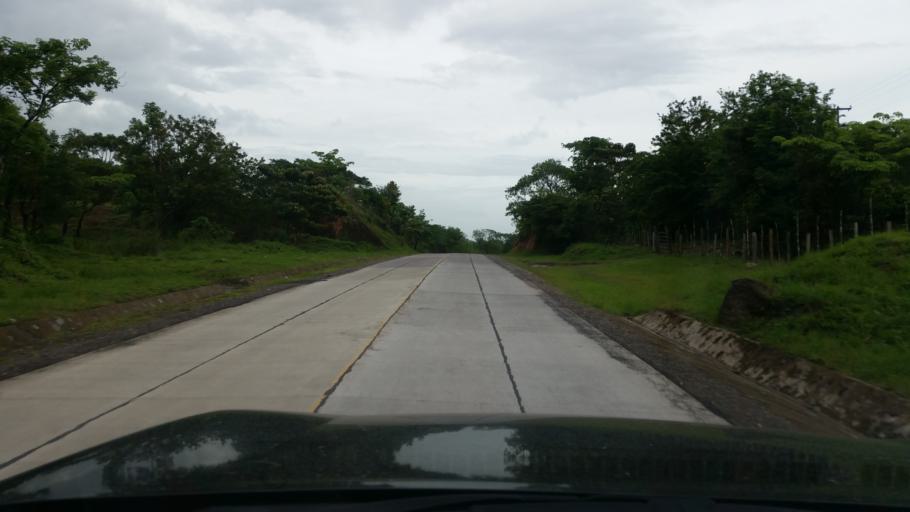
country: NI
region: Matagalpa
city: Rio Blanco
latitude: 13.1509
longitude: -84.9816
